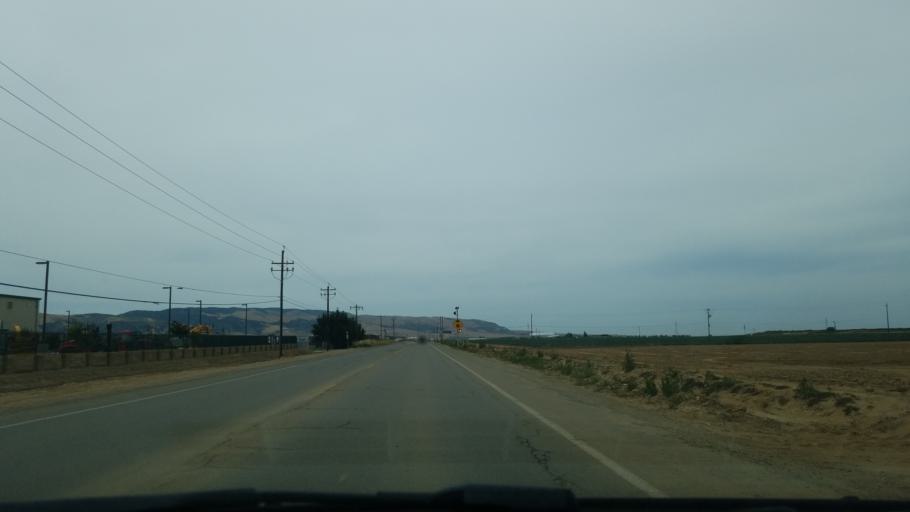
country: US
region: California
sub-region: Santa Barbara County
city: Santa Maria
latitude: 34.9210
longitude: -120.4864
